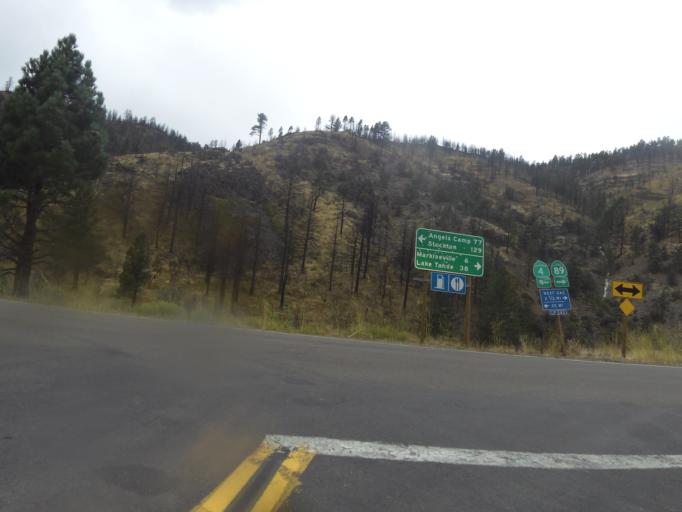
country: US
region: Nevada
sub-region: Douglas County
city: Gardnerville Ranchos
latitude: 38.6606
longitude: -119.7264
